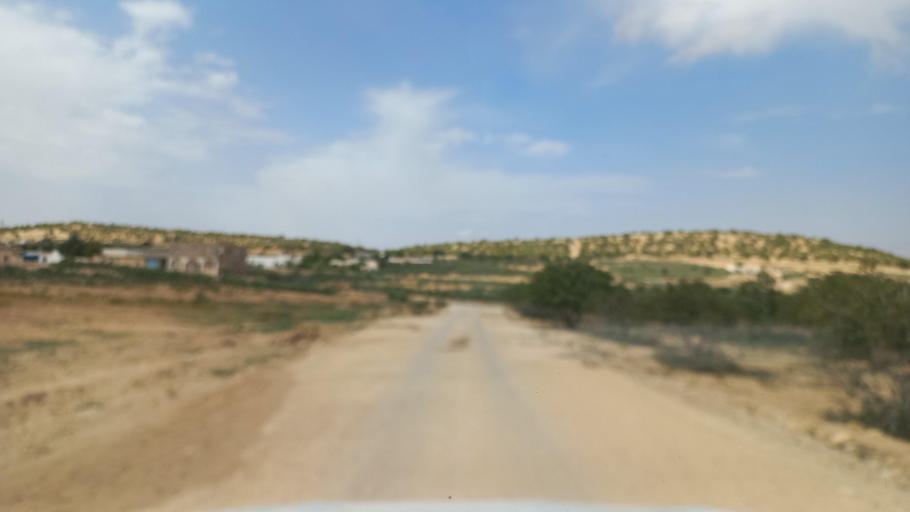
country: TN
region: Al Qasrayn
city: Kasserine
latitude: 35.3875
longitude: 8.8630
